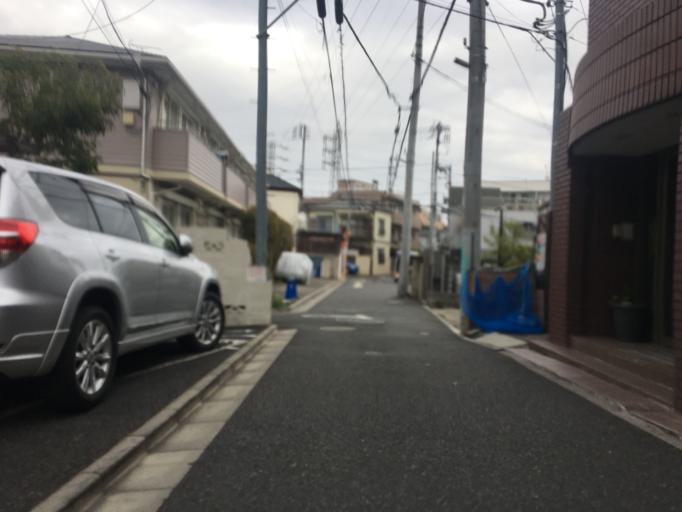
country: JP
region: Tokyo
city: Tokyo
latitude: 35.7189
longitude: 139.6619
